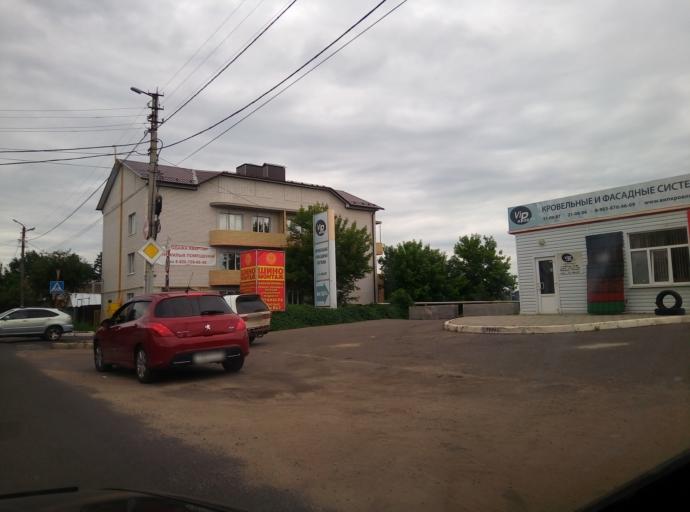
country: RU
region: Kursk
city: Kursk
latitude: 51.7393
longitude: 36.1850
